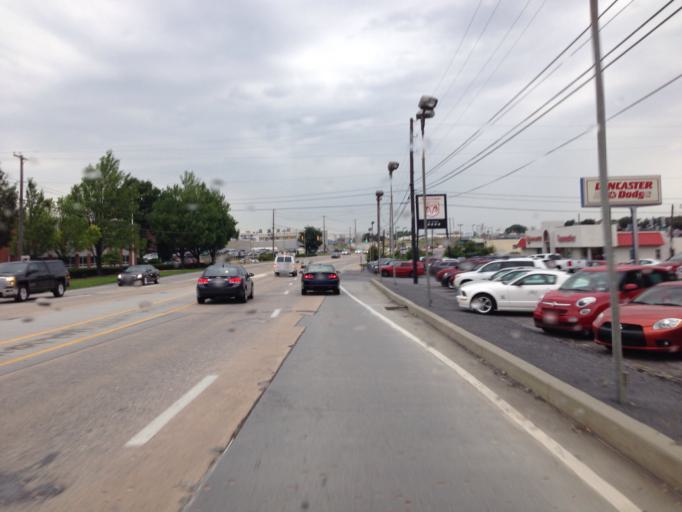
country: US
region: Pennsylvania
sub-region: Lancaster County
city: East Petersburg
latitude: 40.0726
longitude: -76.3346
